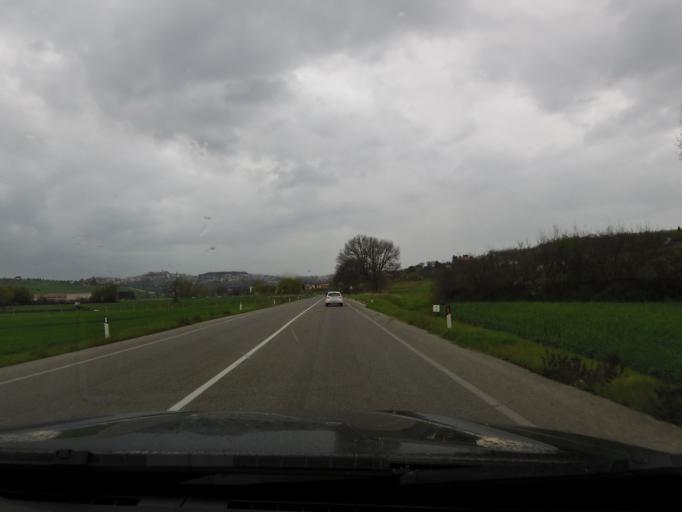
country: IT
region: The Marches
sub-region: Provincia di Ancona
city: Villa Musone
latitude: 43.4568
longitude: 13.5895
